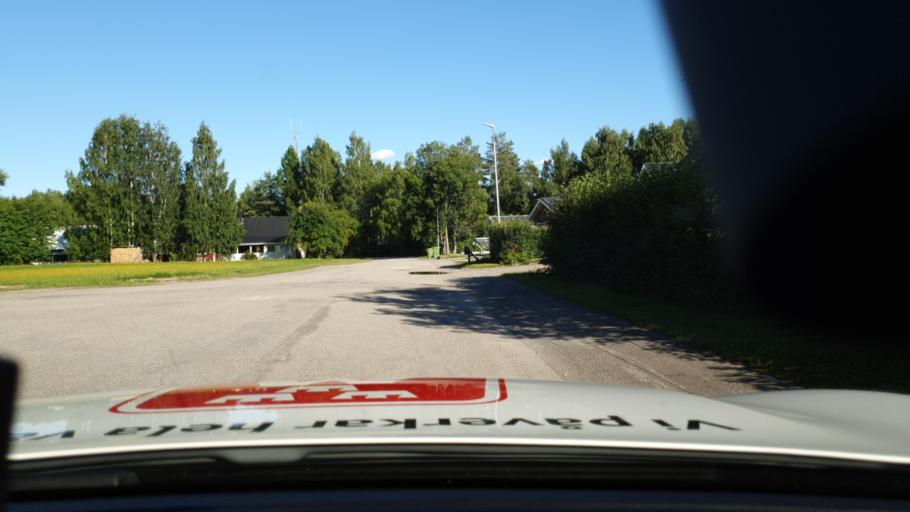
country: SE
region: Norrbotten
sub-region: Alvsbyns Kommun
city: AElvsbyn
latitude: 65.6655
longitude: 20.8616
